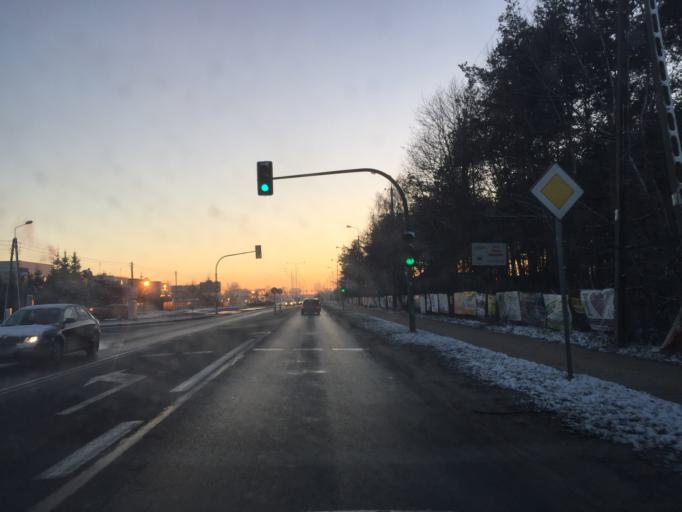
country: PL
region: Kujawsko-Pomorskie
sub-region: Powiat torunski
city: Lubicz Dolny
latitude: 53.0412
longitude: 18.6976
